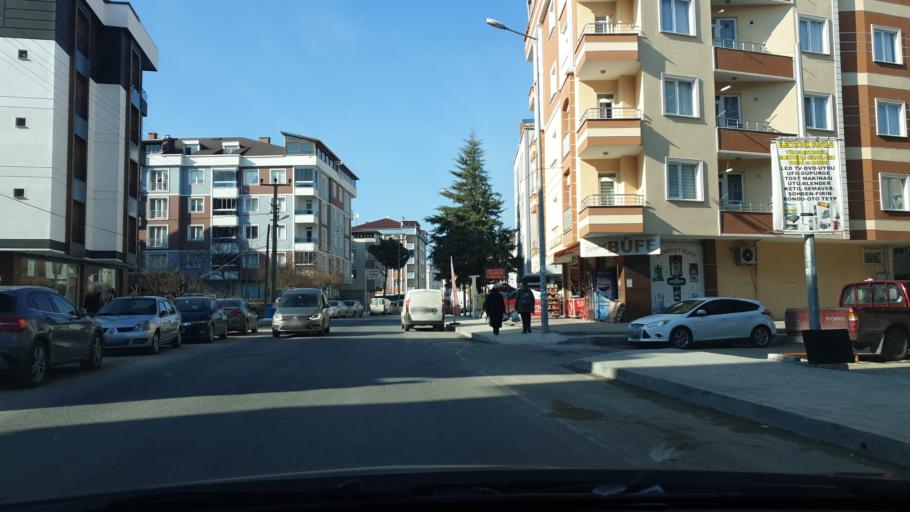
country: TR
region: Tekirdag
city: Cerkezkoey
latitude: 41.2851
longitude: 27.9936
